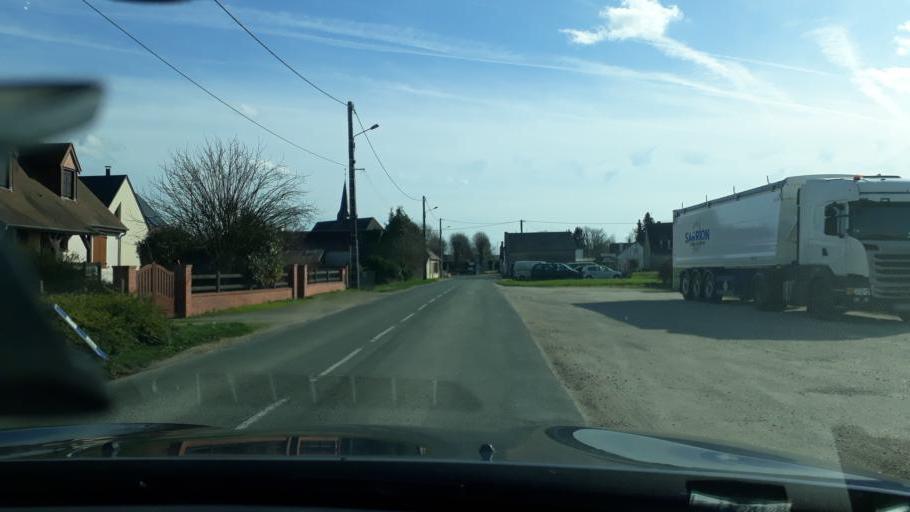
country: FR
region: Centre
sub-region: Departement du Loiret
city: Ascheres-le-Marche
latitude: 48.0708
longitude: 1.9886
